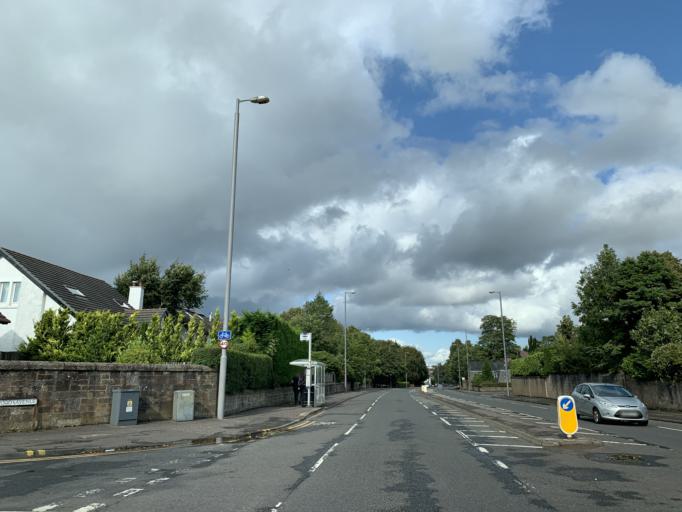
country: GB
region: Scotland
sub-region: East Renfrewshire
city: Newton Mearns
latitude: 55.7810
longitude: -4.3181
